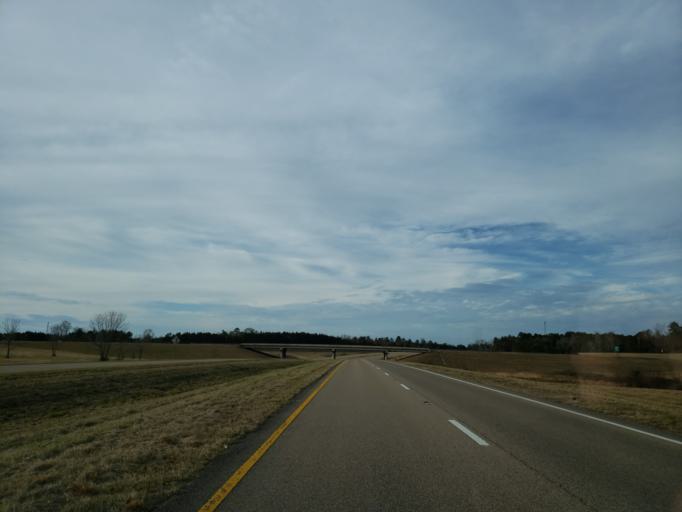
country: US
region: Mississippi
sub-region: Wayne County
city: Waynesboro
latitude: 31.6791
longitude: -88.6130
